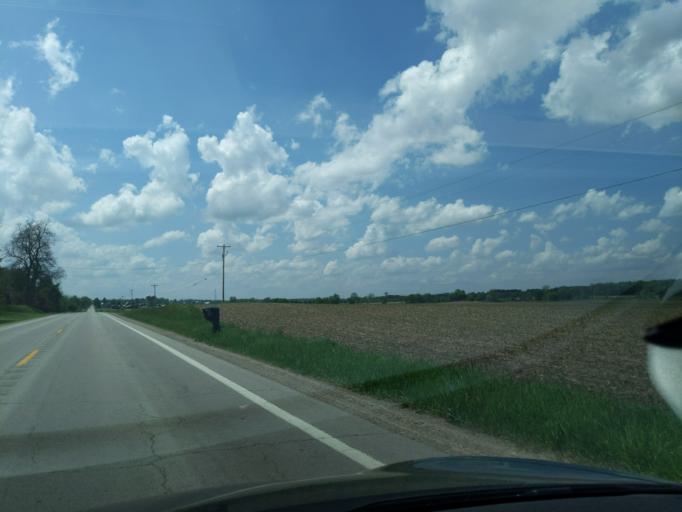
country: US
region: Michigan
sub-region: Ingham County
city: Williamston
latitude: 42.5558
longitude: -84.2747
